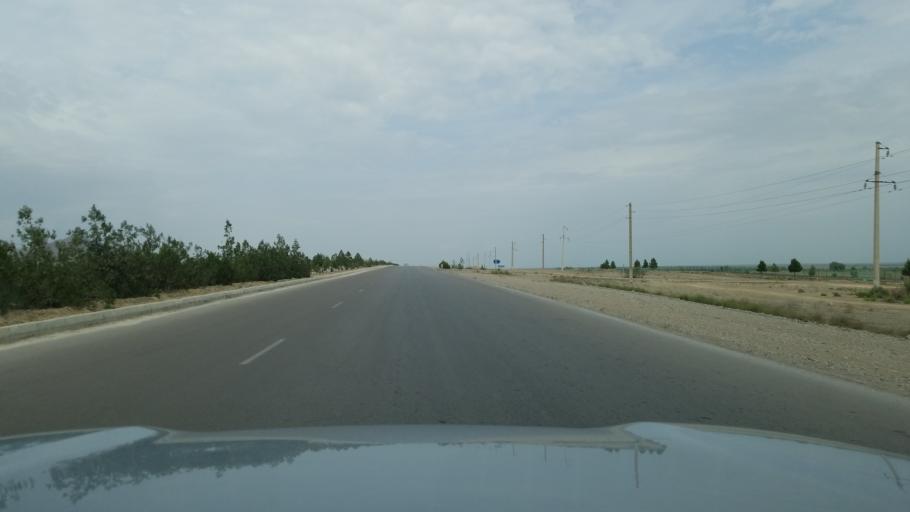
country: TM
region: Ahal
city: Baharly
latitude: 38.2279
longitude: 57.7908
